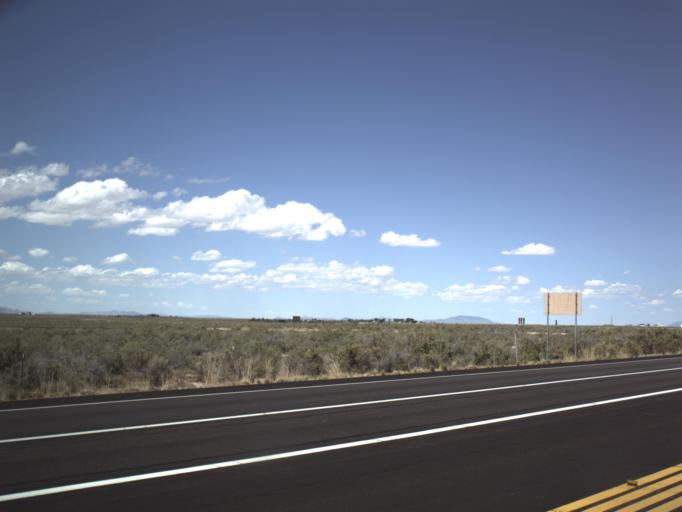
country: US
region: Utah
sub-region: Millard County
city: Delta
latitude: 39.3502
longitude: -112.4965
